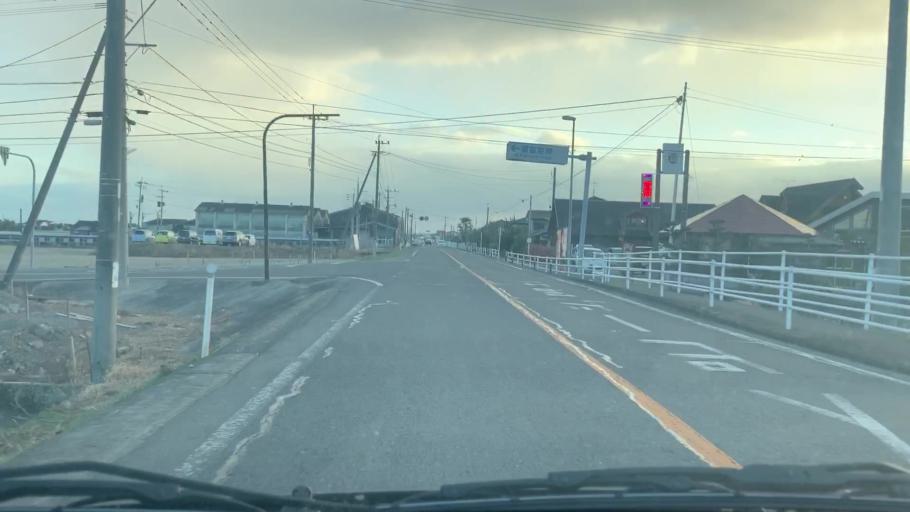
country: JP
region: Saga Prefecture
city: Saga-shi
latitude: 33.1935
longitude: 130.1930
